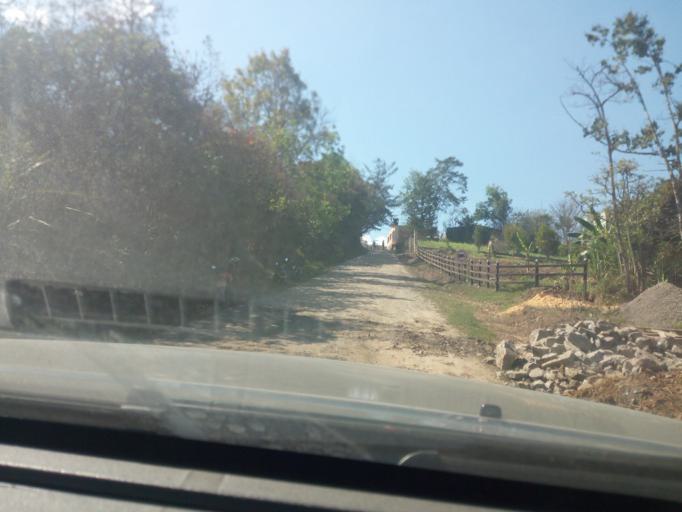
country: CO
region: Boyaca
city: Guateque
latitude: 5.0018
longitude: -73.4691
